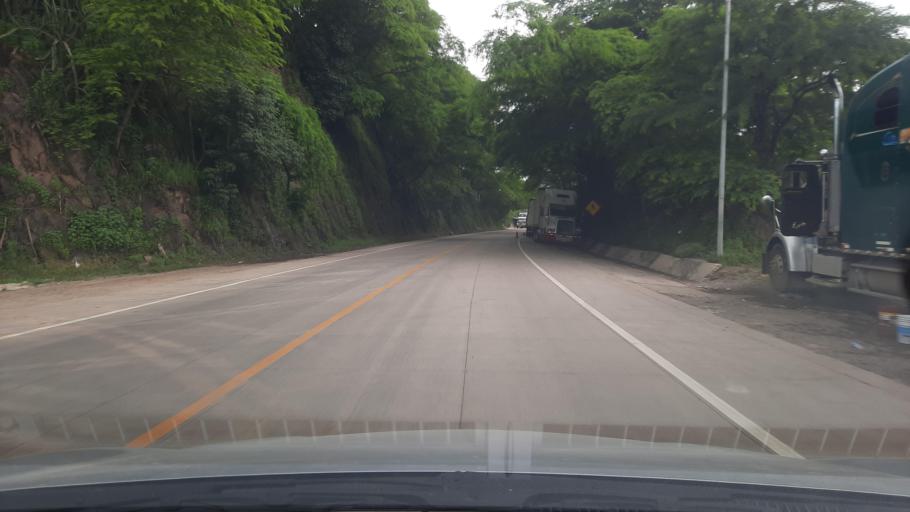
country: NI
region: Chinandega
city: Somotillo
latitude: 12.8640
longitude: -86.8517
